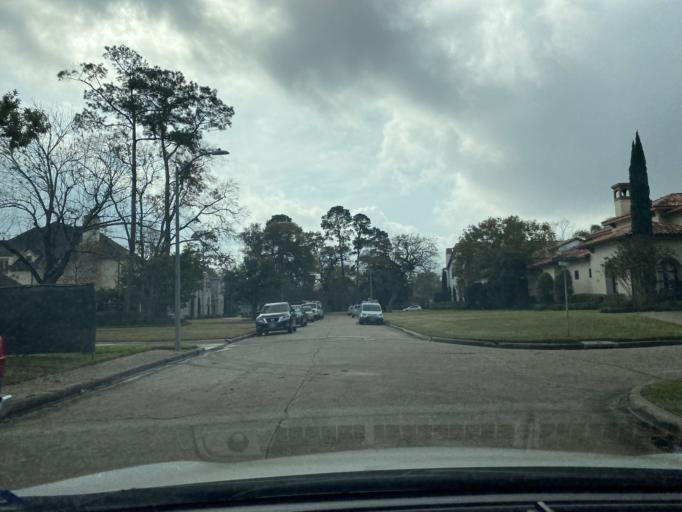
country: US
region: Texas
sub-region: Harris County
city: Hunters Creek Village
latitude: 29.7675
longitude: -95.4753
